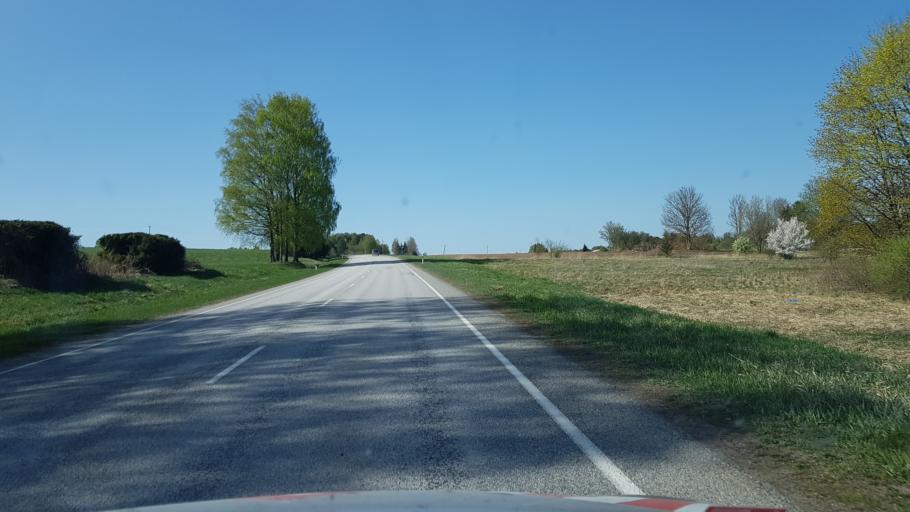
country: EE
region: Valgamaa
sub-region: Torva linn
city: Torva
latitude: 57.9142
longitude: 26.0338
